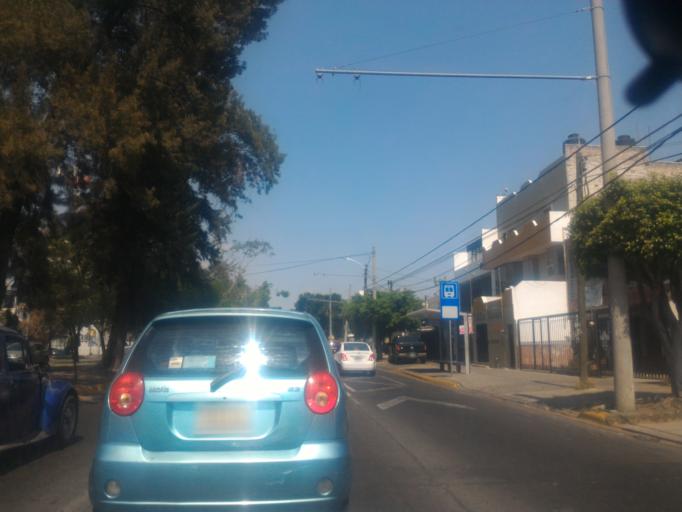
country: MX
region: Jalisco
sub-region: Zapopan
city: Zapopan
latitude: 20.7072
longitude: -103.3570
